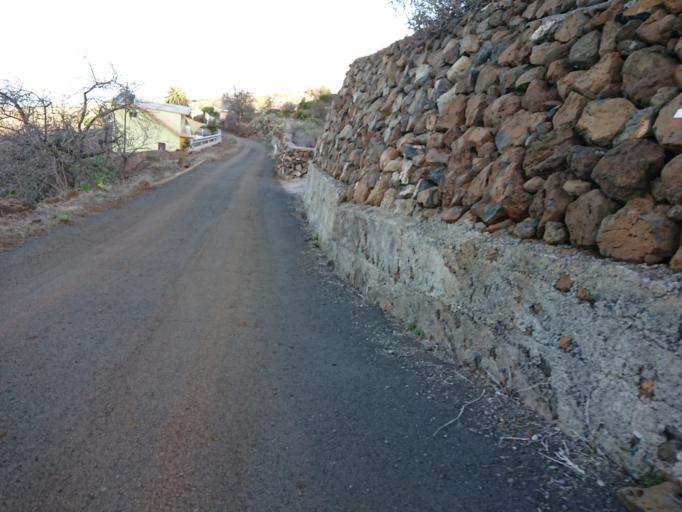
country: ES
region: Canary Islands
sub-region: Provincia de Santa Cruz de Tenerife
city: Tijarafe
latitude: 28.6732
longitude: -17.9421
